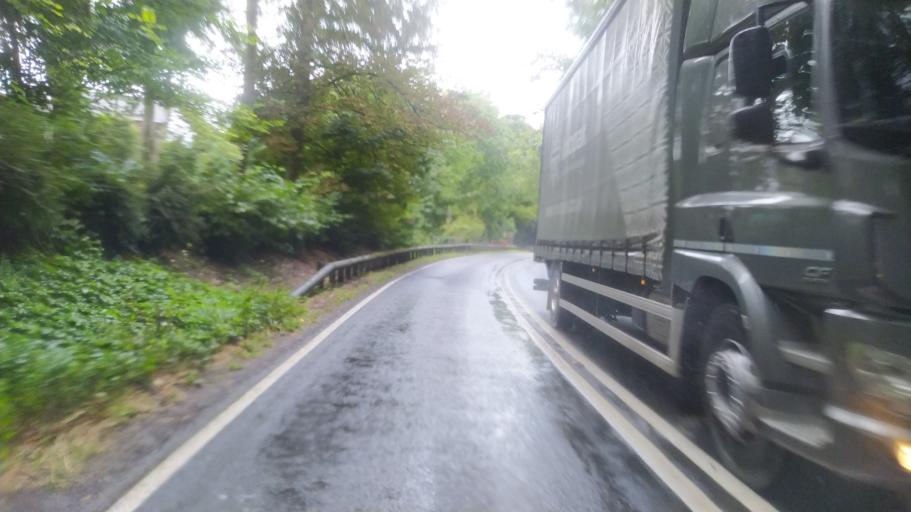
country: GB
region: England
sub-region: Hampshire
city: Swanmore
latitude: 51.0047
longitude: -1.1097
